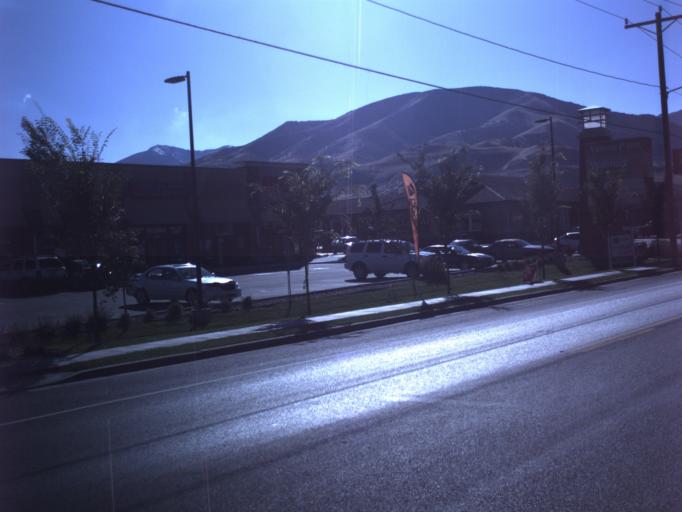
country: US
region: Utah
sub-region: Salt Lake County
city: Magna
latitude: 40.6965
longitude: -112.0882
